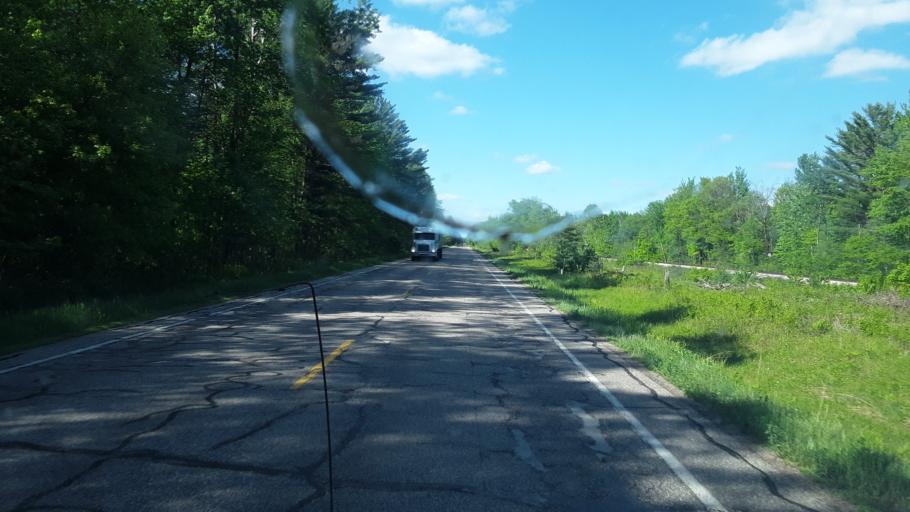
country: US
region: Wisconsin
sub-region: Wood County
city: Nekoosa
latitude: 44.2733
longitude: -90.1385
